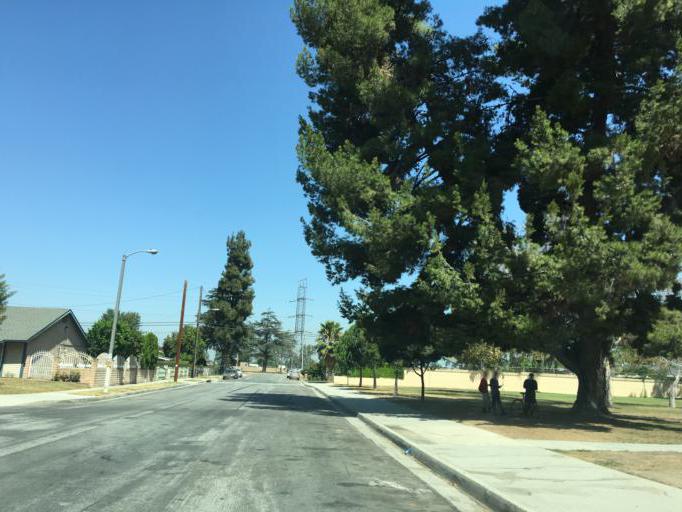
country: US
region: California
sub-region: Los Angeles County
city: Avocado Heights
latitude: 34.0491
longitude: -118.0033
